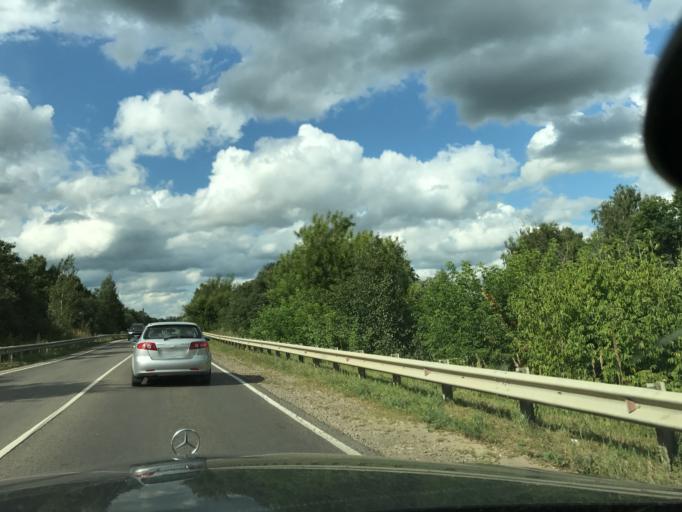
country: RU
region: Vladimir
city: Sobinka
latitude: 56.0086
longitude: 39.9981
